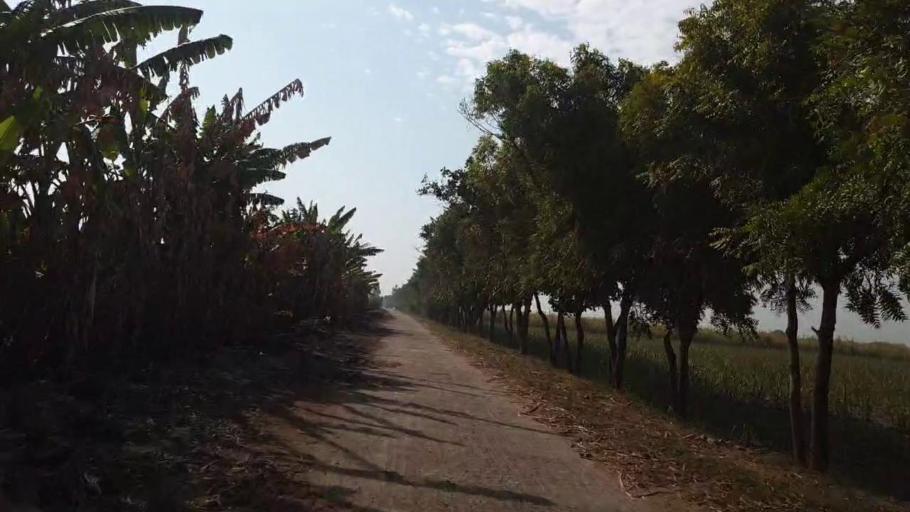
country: PK
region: Sindh
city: Matiari
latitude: 25.5556
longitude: 68.5159
